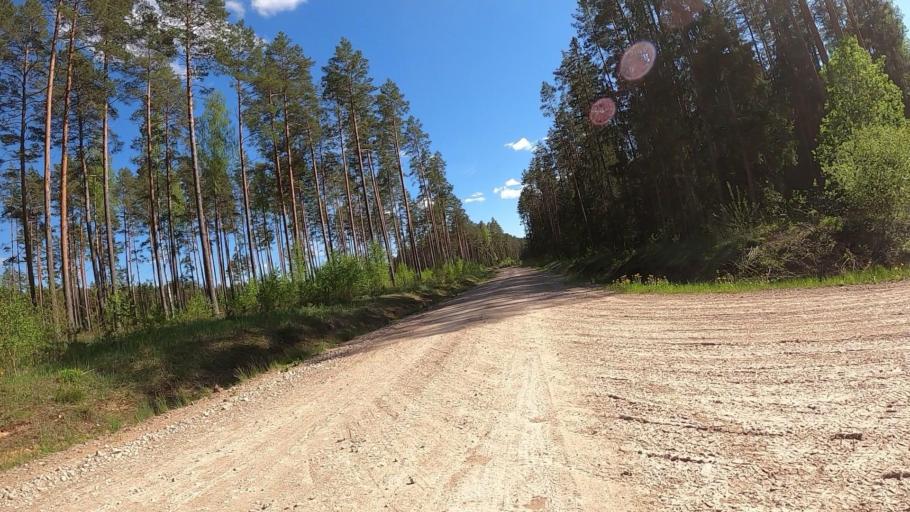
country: LV
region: Baldone
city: Baldone
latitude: 56.7754
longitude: 24.3745
